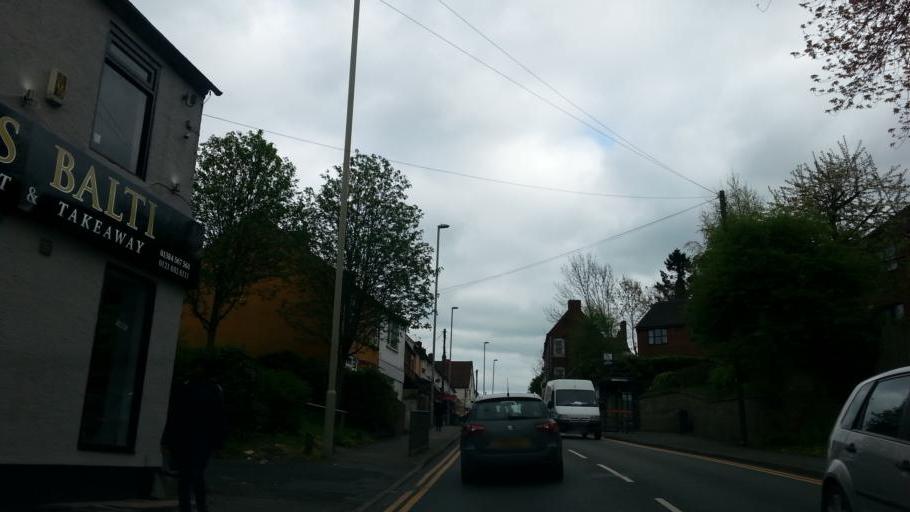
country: GB
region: England
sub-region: Sandwell
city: Cradley Heath
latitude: 52.4586
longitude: -2.0839
